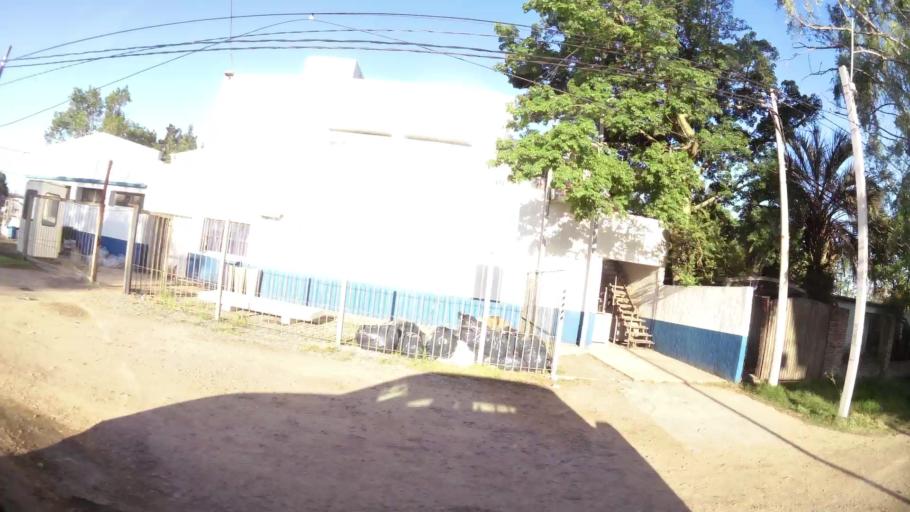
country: UY
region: Canelones
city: Paso de Carrasco
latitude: -34.8473
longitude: -56.0278
